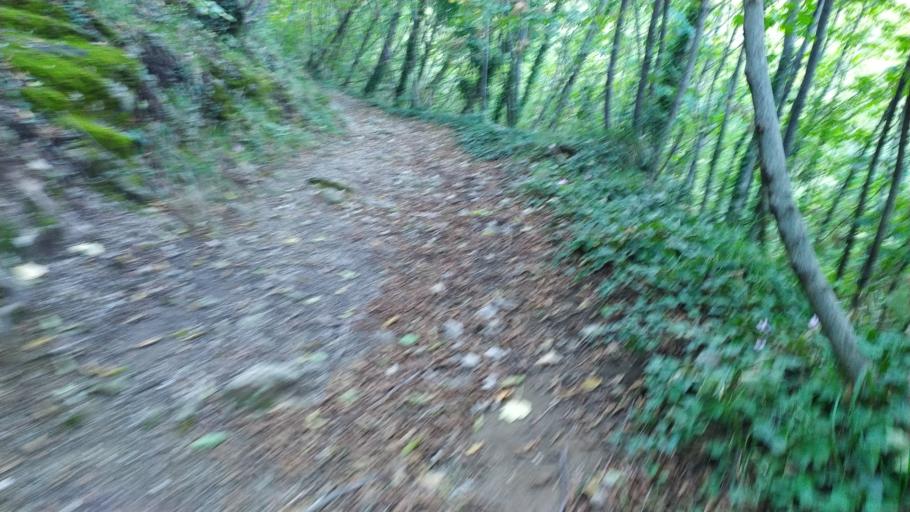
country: IT
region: Campania
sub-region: Provincia di Salerno
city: Nocera Superiore
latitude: 40.7203
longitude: 14.6821
